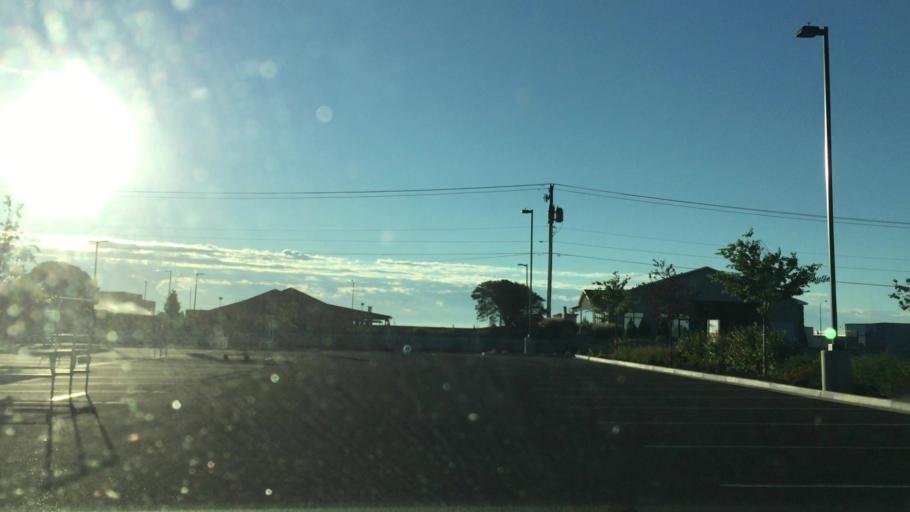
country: US
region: Washington
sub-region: Grant County
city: Moses Lake
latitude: 47.1411
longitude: -119.2807
